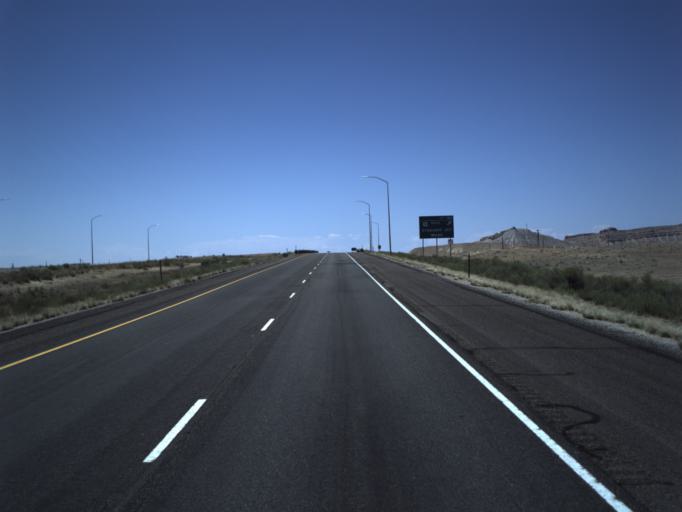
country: US
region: Utah
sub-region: Grand County
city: Moab
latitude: 38.9440
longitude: -109.8075
